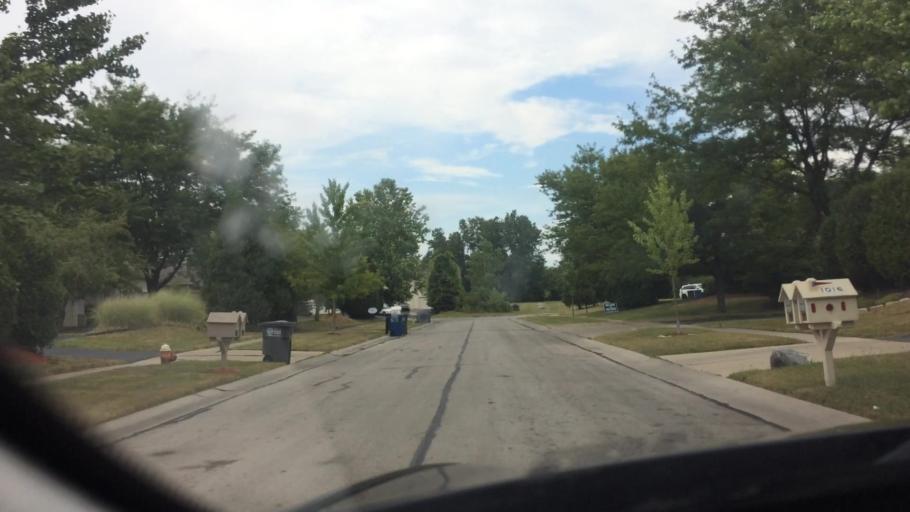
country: US
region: Ohio
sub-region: Lucas County
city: Ottawa Hills
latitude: 41.6499
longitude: -83.6557
